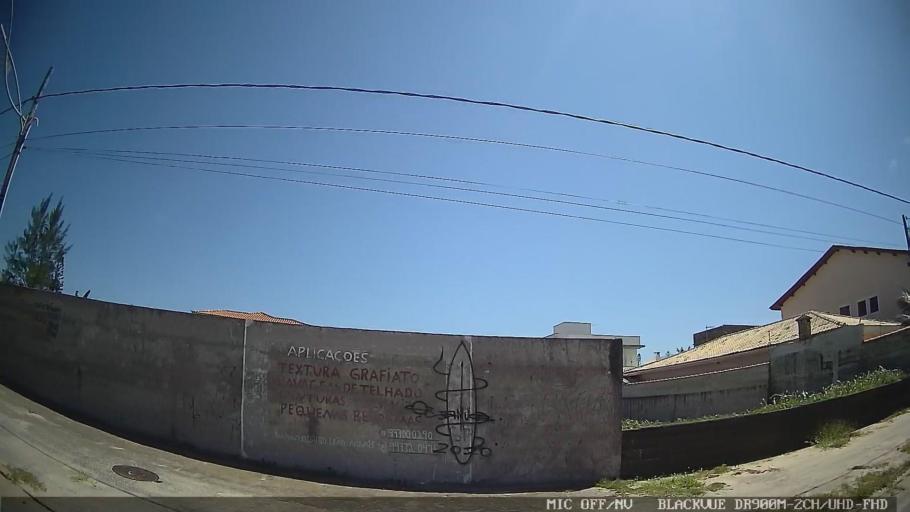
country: BR
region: Sao Paulo
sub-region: Peruibe
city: Peruibe
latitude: -24.3110
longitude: -46.9782
